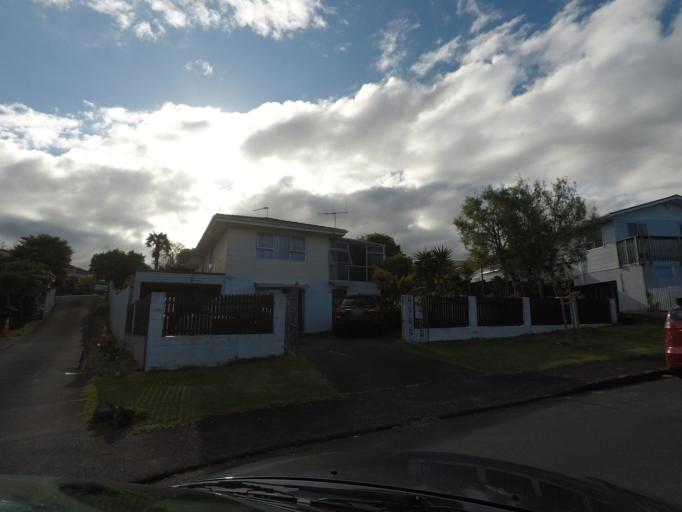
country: NZ
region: Auckland
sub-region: Auckland
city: Rosebank
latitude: -36.8806
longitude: 174.6548
